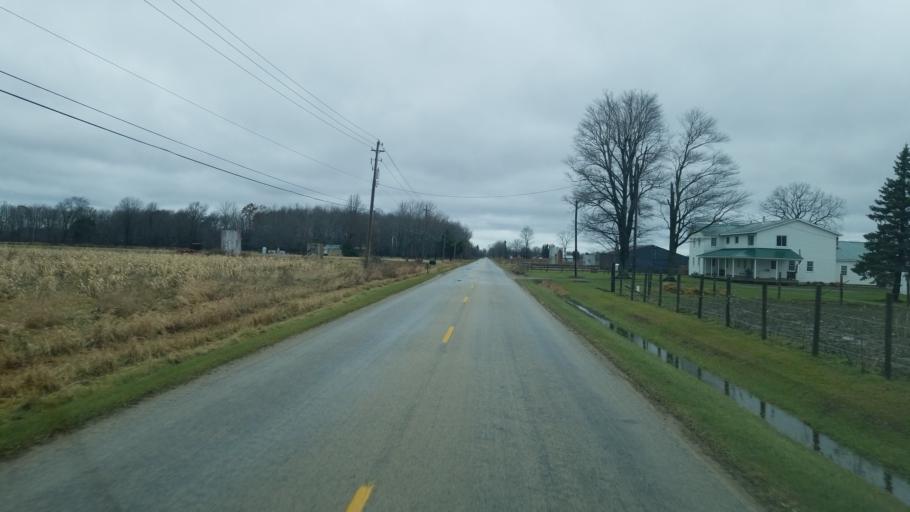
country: US
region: Ohio
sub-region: Ashtabula County
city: North Kingsville
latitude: 41.7727
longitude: -80.6232
